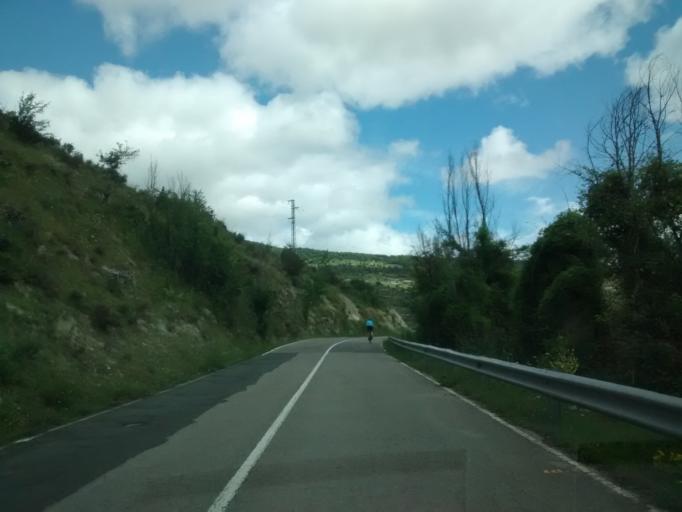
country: ES
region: La Rioja
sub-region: Provincia de La Rioja
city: Terroba
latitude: 42.2484
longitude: -2.4535
